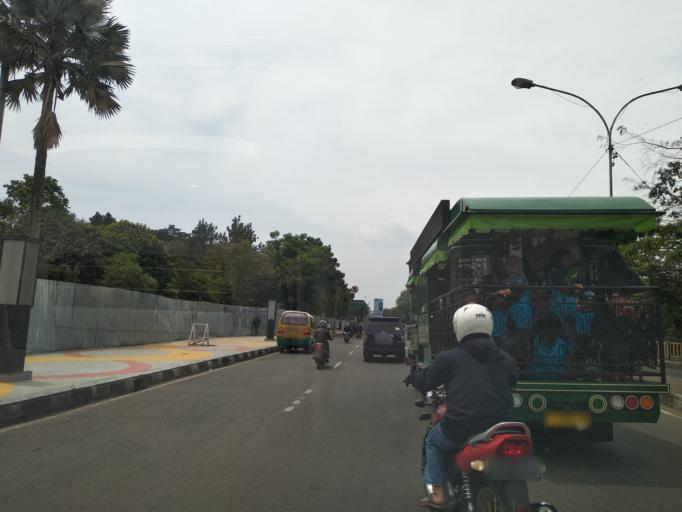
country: ID
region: West Java
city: Bandung
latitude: -6.9374
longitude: 107.6044
